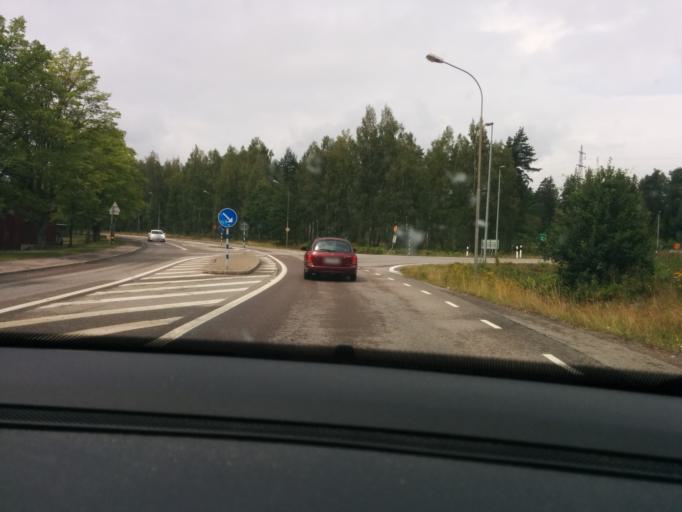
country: SE
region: Kronoberg
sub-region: Vaxjo Kommun
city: Vaexjoe
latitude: 56.8997
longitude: 14.7960
